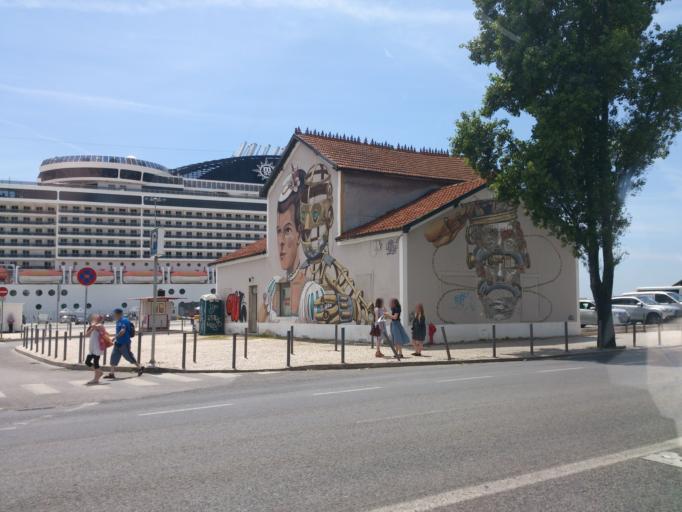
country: PT
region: Lisbon
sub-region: Lisbon
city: Lisbon
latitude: 38.7102
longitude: -9.1280
